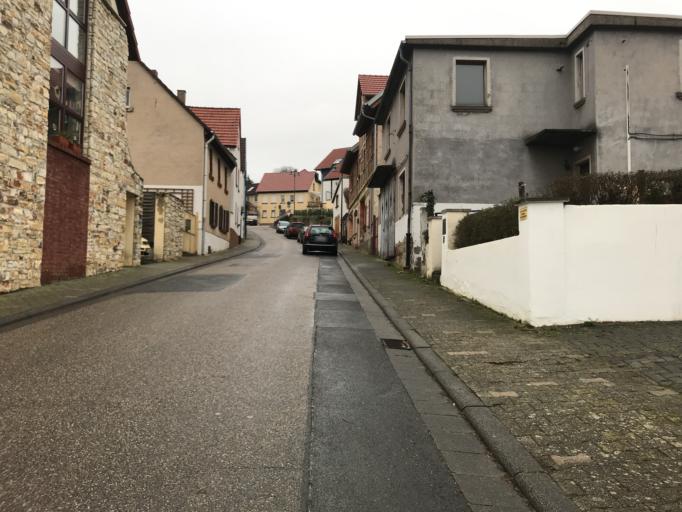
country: DE
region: Rheinland-Pfalz
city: Sorgenloch
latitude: 49.8816
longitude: 8.1996
